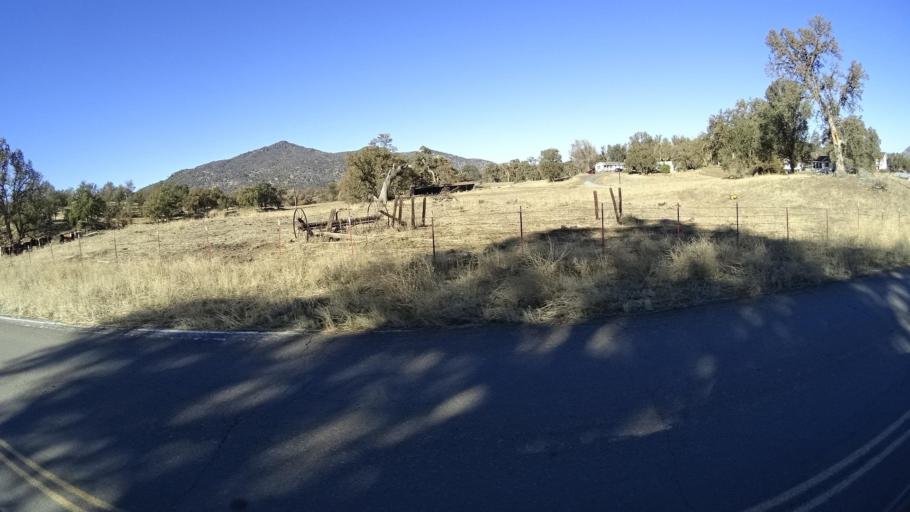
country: US
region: California
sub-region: Kern County
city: Alta Sierra
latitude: 35.7578
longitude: -118.7142
